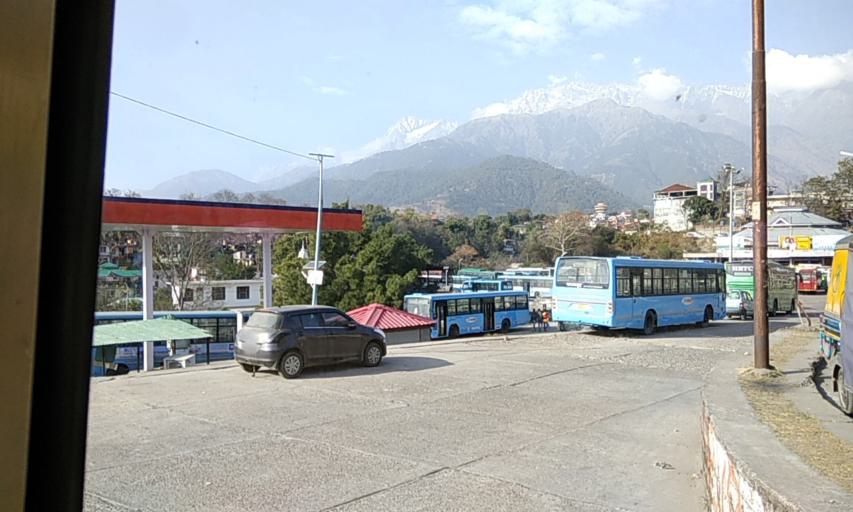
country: IN
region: Himachal Pradesh
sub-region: Kangra
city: Palampur
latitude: 32.1022
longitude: 76.5337
